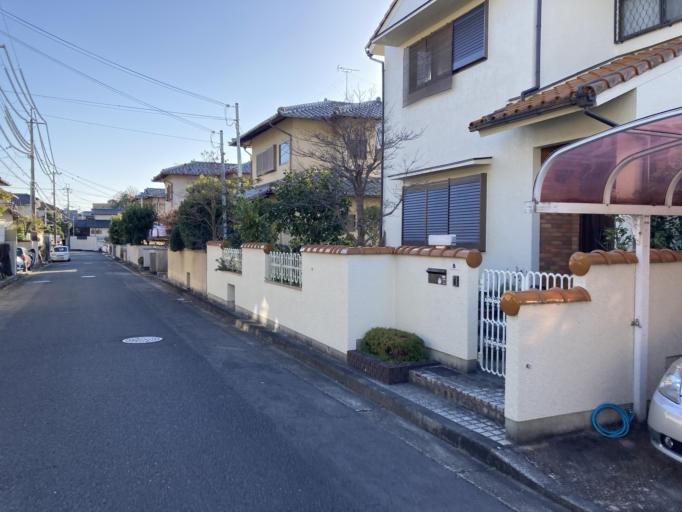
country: JP
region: Nara
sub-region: Ikoma-shi
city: Ikoma
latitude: 34.6769
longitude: 135.7150
